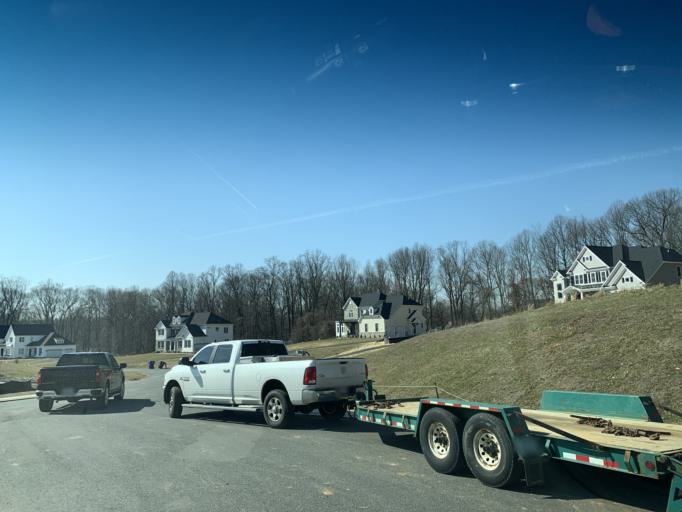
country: US
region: Maryland
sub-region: Harford County
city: Fallston
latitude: 39.5194
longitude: -76.4404
